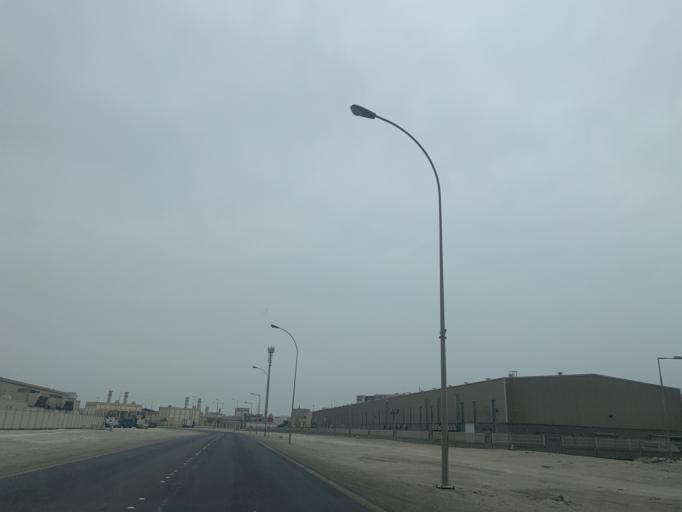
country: BH
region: Muharraq
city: Al Hadd
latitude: 26.2107
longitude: 50.6699
